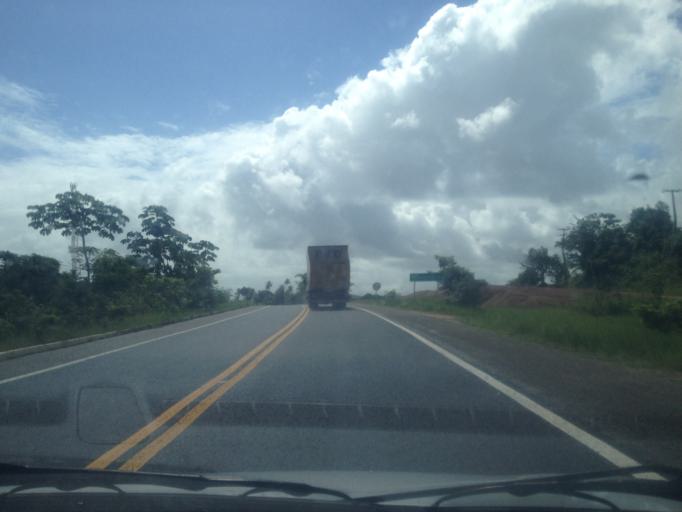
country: BR
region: Sergipe
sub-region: Indiaroba
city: Indiaroba
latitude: -11.6213
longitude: -37.5354
